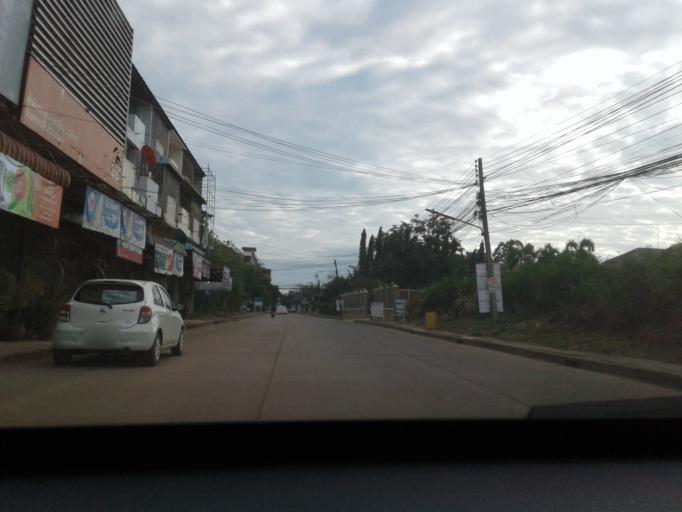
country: TH
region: Changwat Udon Thani
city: Udon Thani
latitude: 17.4291
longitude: 102.7842
